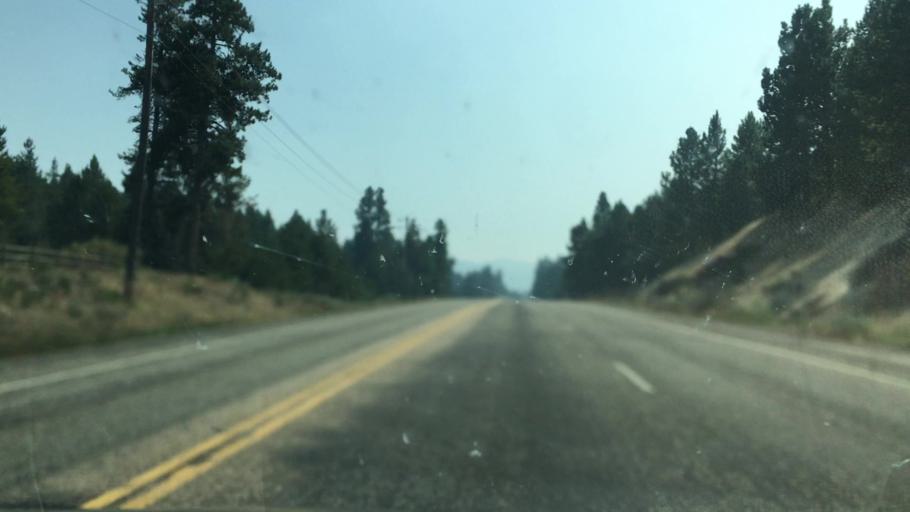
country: US
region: Idaho
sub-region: Valley County
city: Cascade
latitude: 44.3761
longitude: -116.0152
